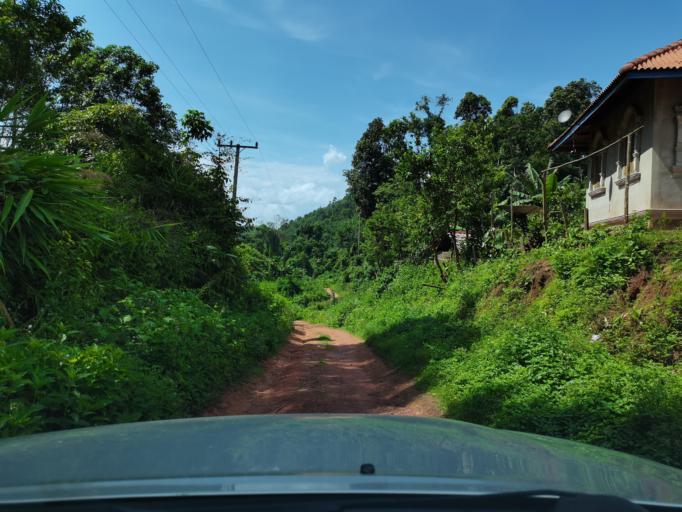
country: LA
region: Loungnamtha
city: Muang Nale
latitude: 20.5304
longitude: 101.0648
